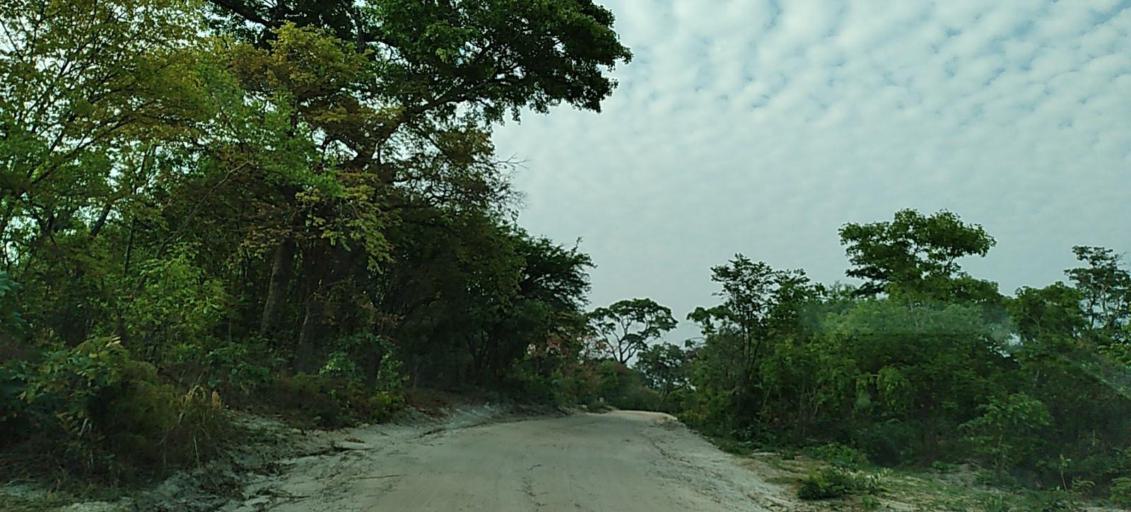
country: ZM
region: Copperbelt
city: Kalulushi
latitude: -12.8939
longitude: 27.6882
